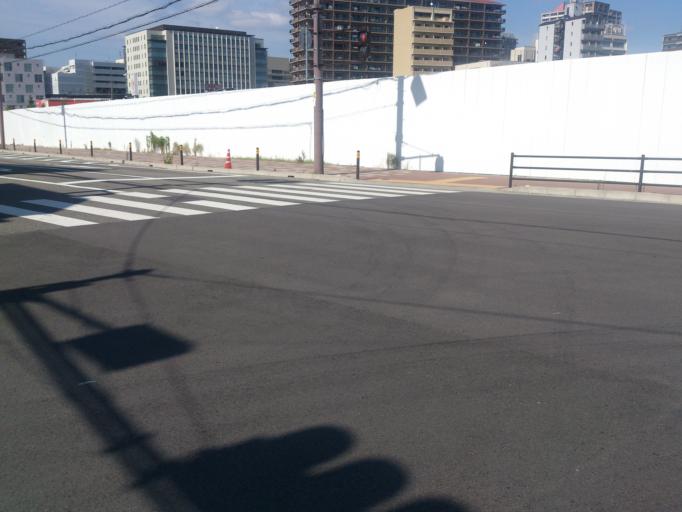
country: JP
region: Hyogo
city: Amagasaki
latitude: 34.7299
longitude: 135.4283
